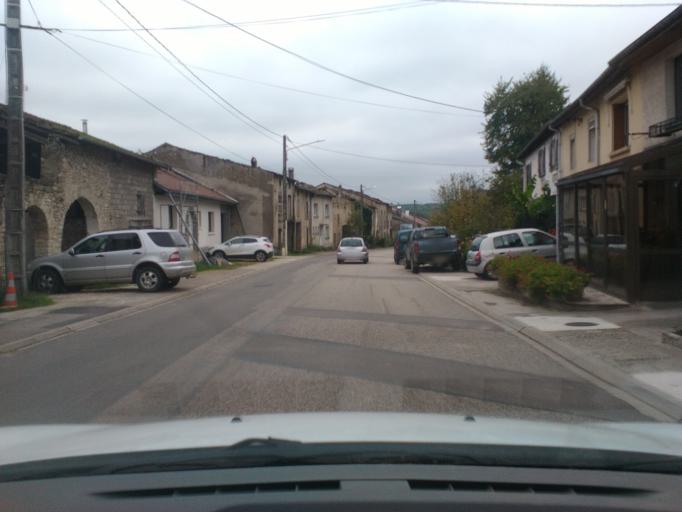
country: FR
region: Lorraine
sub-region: Departement des Vosges
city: Vincey
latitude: 48.2997
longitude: 6.3080
